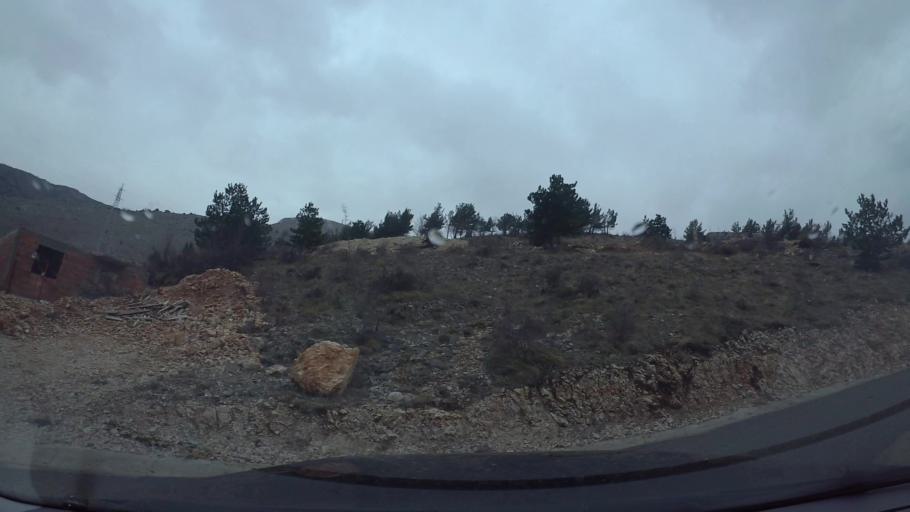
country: BA
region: Federation of Bosnia and Herzegovina
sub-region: Hercegovacko-Bosanski Kanton
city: Mostar
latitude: 43.3609
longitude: 17.8249
